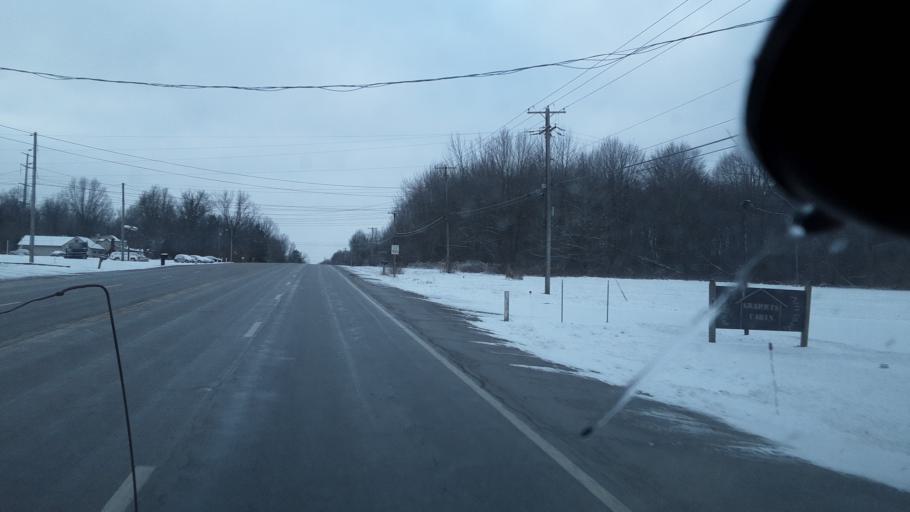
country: US
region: Ohio
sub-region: Trumbull County
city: Lordstown
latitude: 41.1409
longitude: -80.8572
